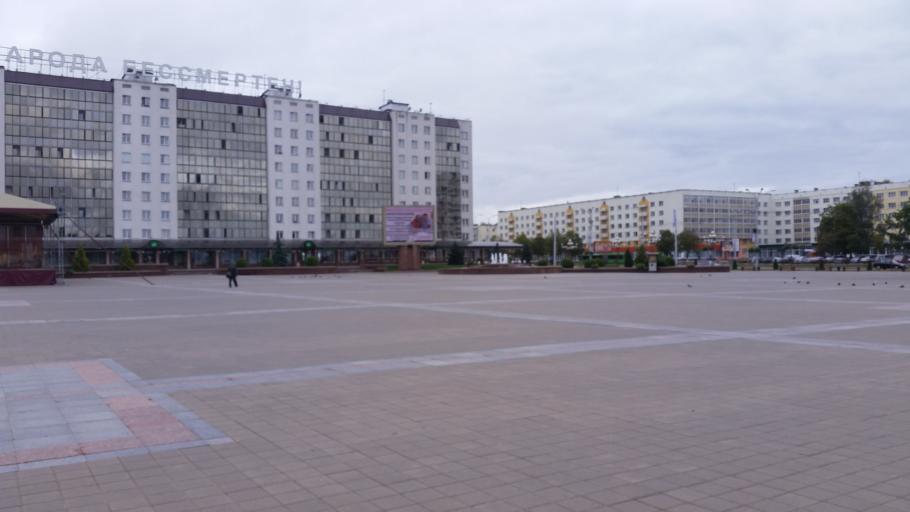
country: BY
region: Vitebsk
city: Vitebsk
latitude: 55.1839
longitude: 30.2043
